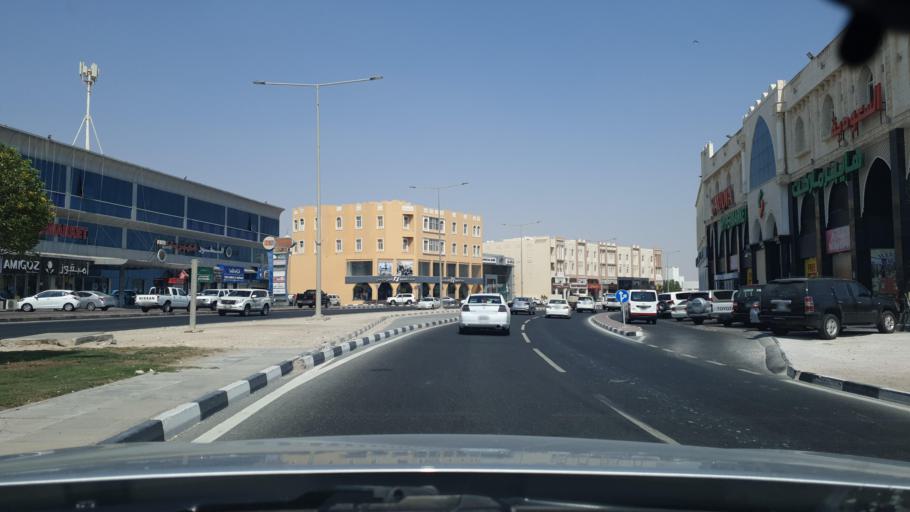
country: QA
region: Al Khawr
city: Al Khawr
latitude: 25.6860
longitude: 51.4954
